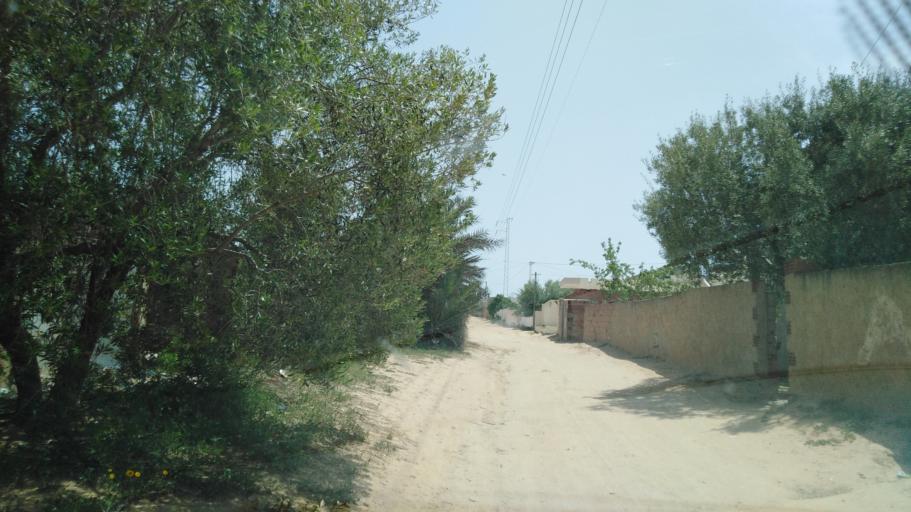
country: TN
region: Safaqis
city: Sfax
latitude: 34.7322
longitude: 10.5509
